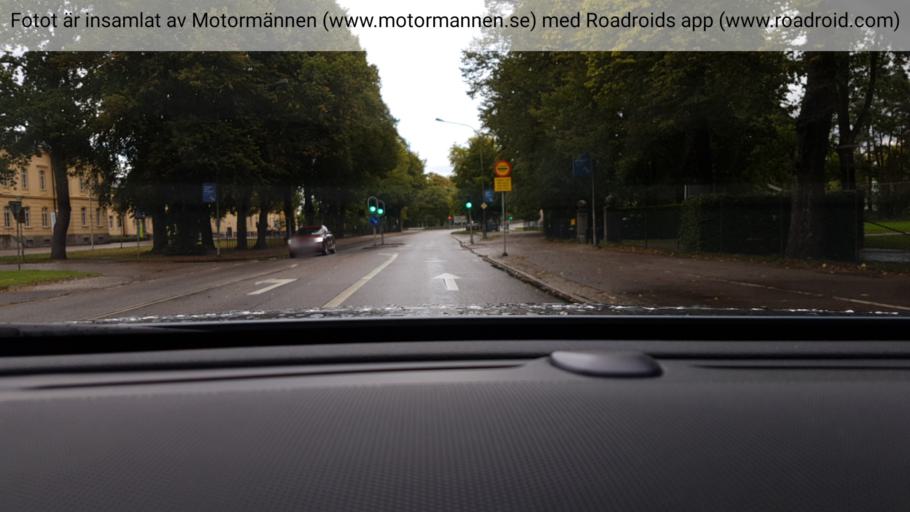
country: SE
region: Vaestra Goetaland
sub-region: Vanersborgs Kommun
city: Vanersborg
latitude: 58.3722
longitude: 12.3221
